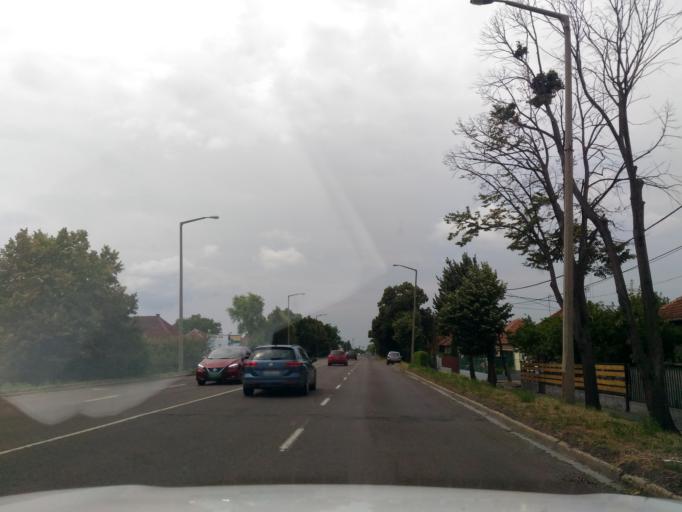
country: HU
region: Jasz-Nagykun-Szolnok
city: Szolnok
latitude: 47.1767
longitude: 20.1597
